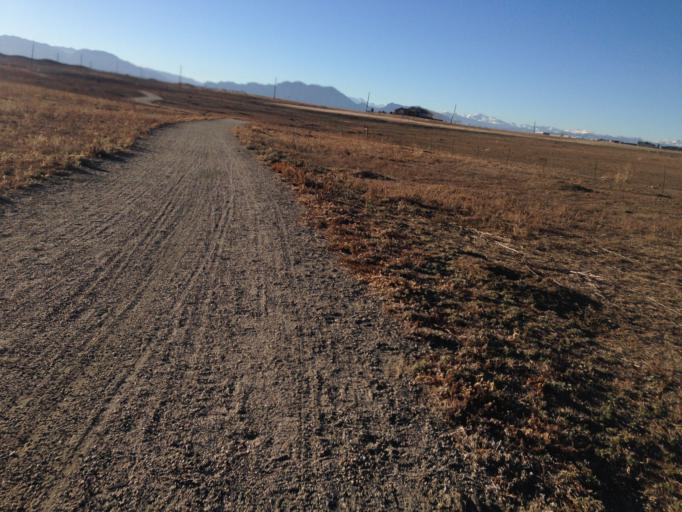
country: US
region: Colorado
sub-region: Broomfield County
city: Broomfield
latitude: 39.9359
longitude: -105.1145
